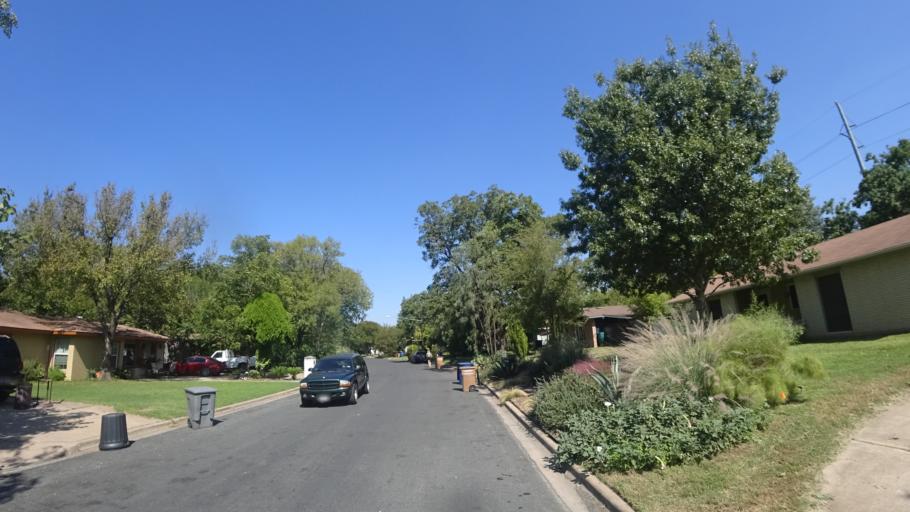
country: US
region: Texas
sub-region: Travis County
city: Austin
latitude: 30.3144
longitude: -97.6856
